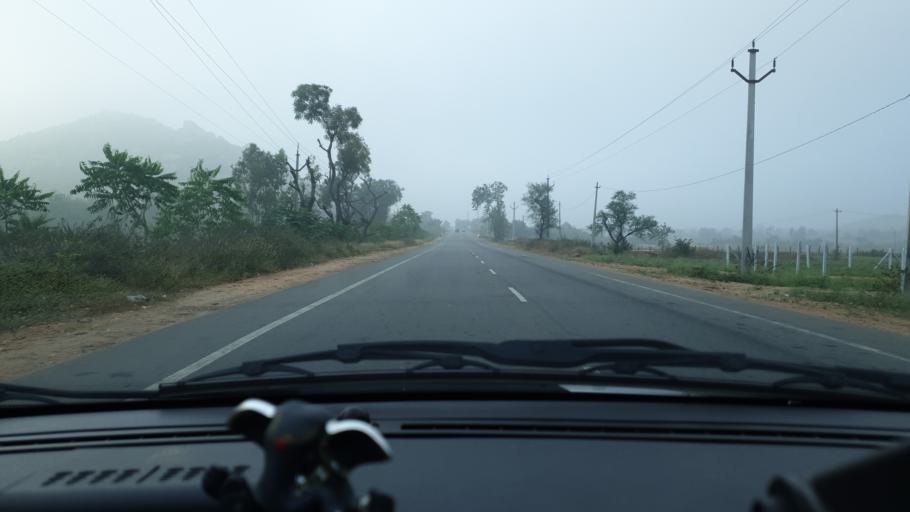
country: IN
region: Telangana
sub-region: Mahbubnagar
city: Farrukhnagar
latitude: 16.8994
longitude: 78.5306
